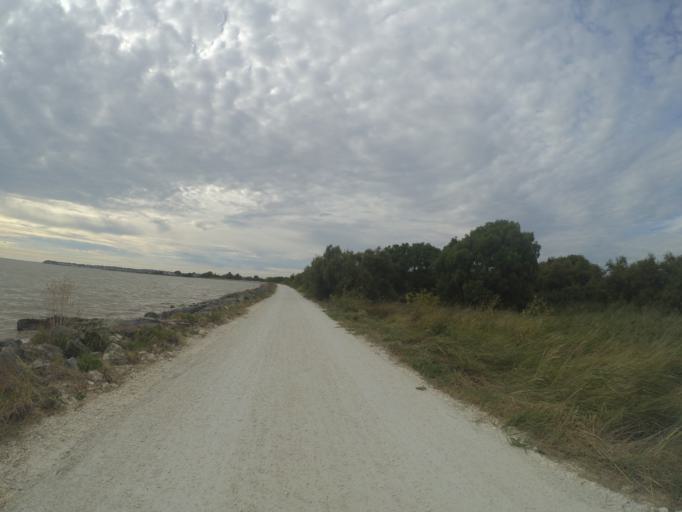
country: FR
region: Poitou-Charentes
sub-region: Departement de la Charente-Maritime
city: Meschers-sur-Gironde
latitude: 45.5485
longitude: -0.9141
